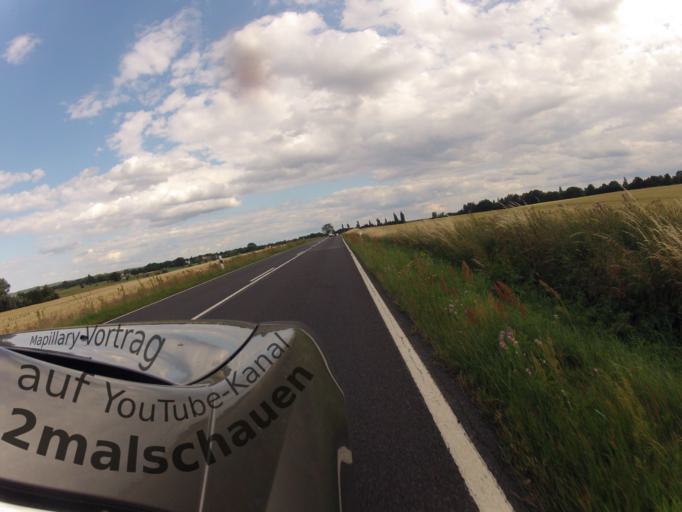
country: DE
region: Mecklenburg-Vorpommern
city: Seebad Bansin
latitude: 53.8912
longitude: 14.0764
